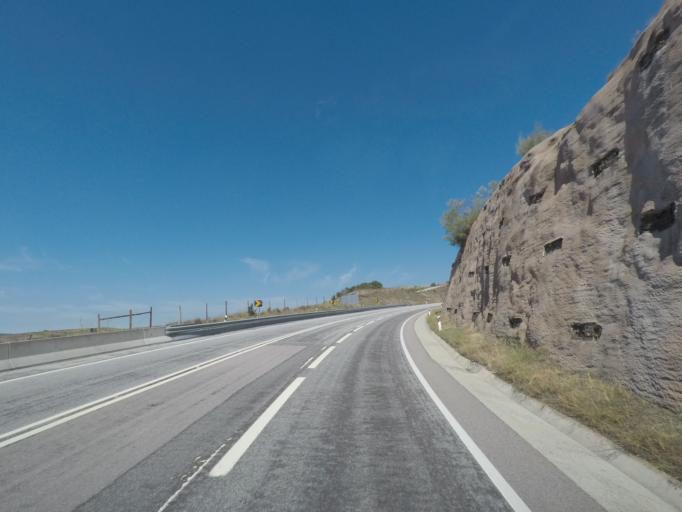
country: PT
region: Braganca
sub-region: Alfandega da Fe
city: Alfandega da Fe
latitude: 41.2770
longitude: -6.8936
